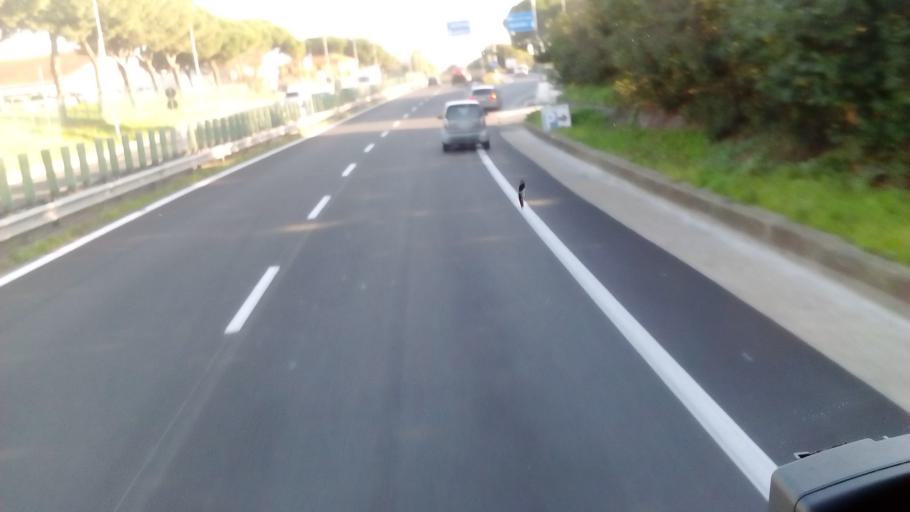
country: IT
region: Latium
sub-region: Citta metropolitana di Roma Capitale
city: Ciampino
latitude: 41.7908
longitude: 12.5939
